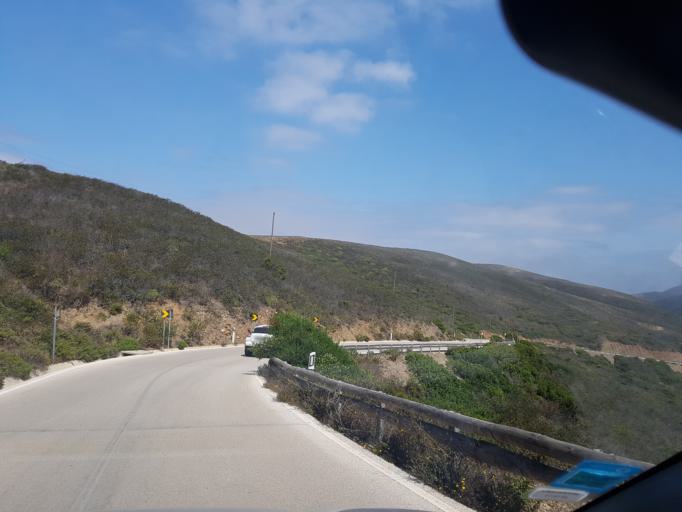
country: PT
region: Faro
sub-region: Vila do Bispo
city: Vila do Bispo
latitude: 37.0990
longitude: -8.9366
